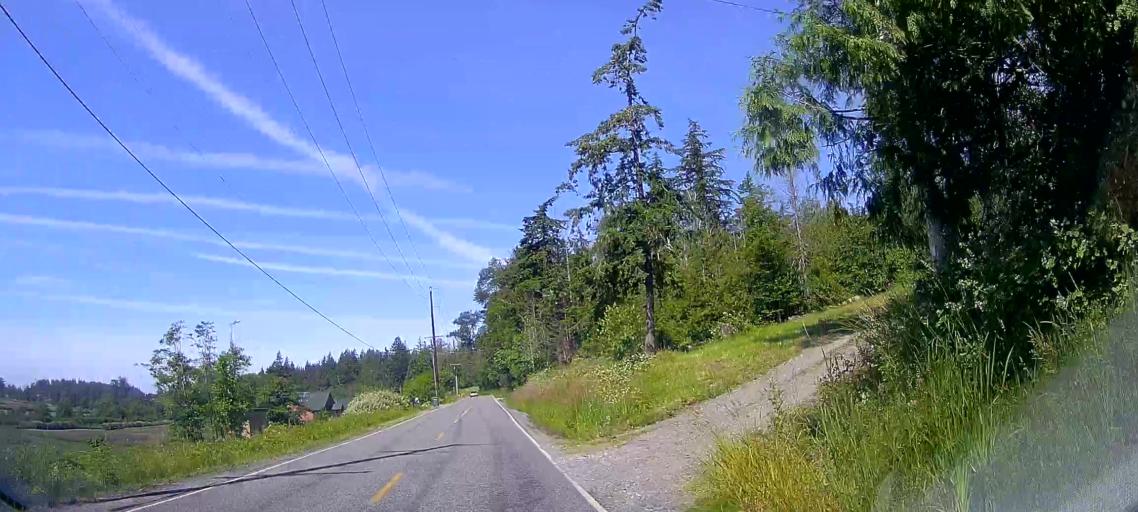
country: US
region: Washington
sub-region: Skagit County
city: Sedro-Woolley
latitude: 48.5348
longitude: -122.2936
